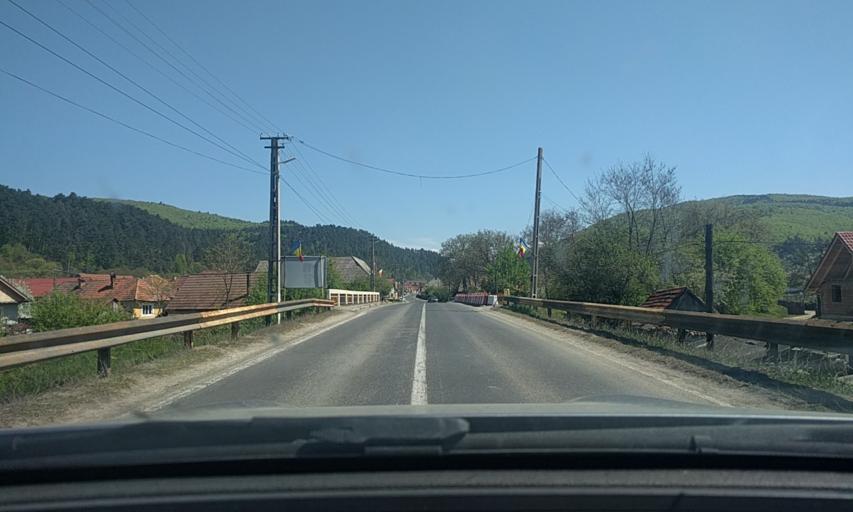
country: RO
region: Brasov
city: Tunelu-Teliu
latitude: 45.7035
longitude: 25.8457
